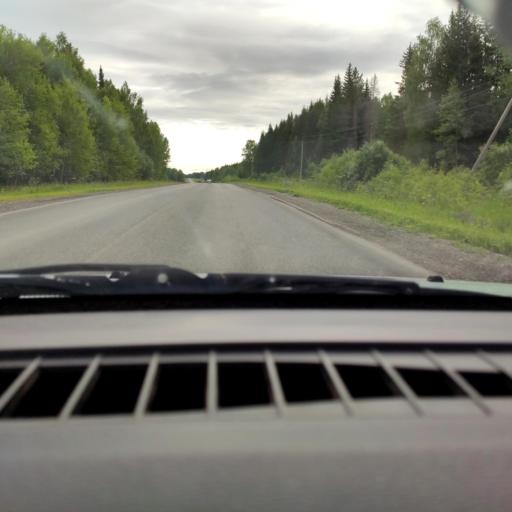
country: RU
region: Perm
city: Orda
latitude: 57.2338
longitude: 56.9738
